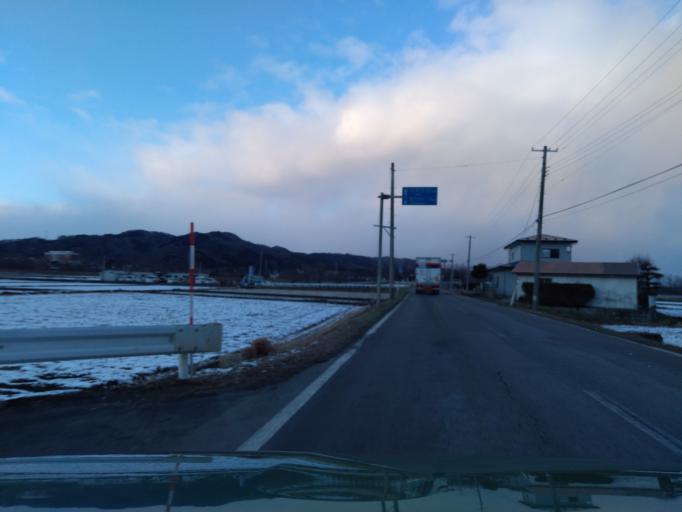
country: JP
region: Iwate
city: Shizukuishi
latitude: 39.6917
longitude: 141.0653
